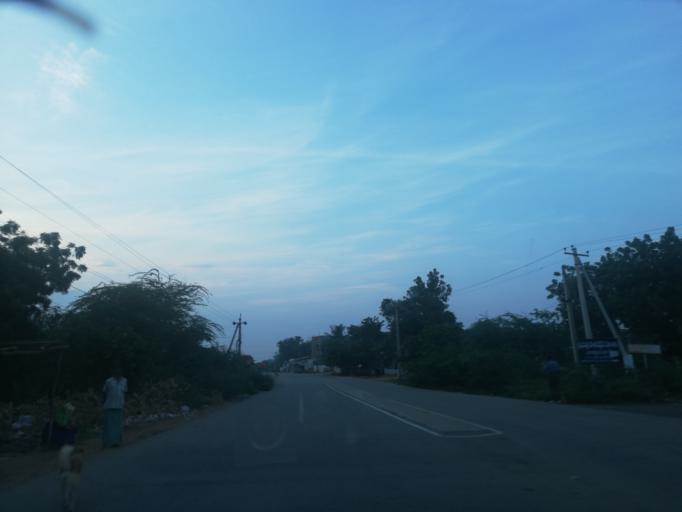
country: IN
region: Andhra Pradesh
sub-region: Guntur
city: Macherla
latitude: 16.5925
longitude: 79.3158
